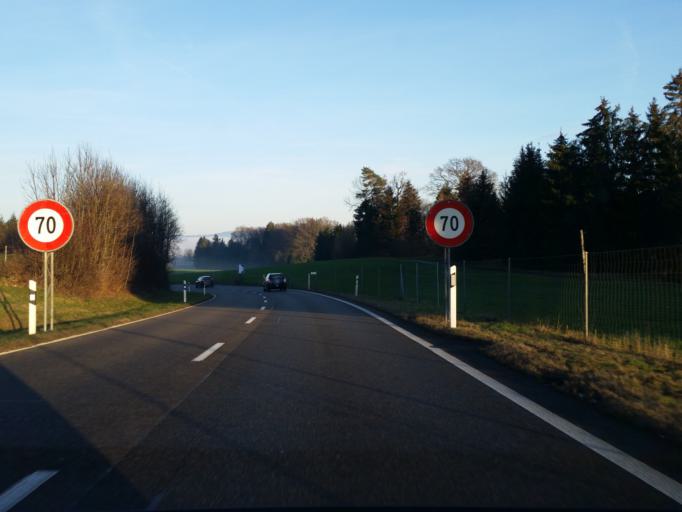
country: CH
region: Saint Gallen
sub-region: Wahlkreis Rorschach
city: Morschwil
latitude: 47.4678
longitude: 9.4436
